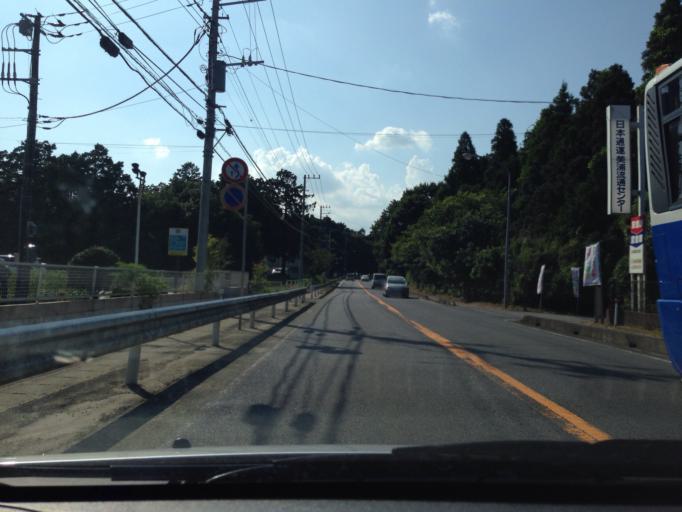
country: JP
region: Ibaraki
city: Inashiki
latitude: 36.0050
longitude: 140.3061
